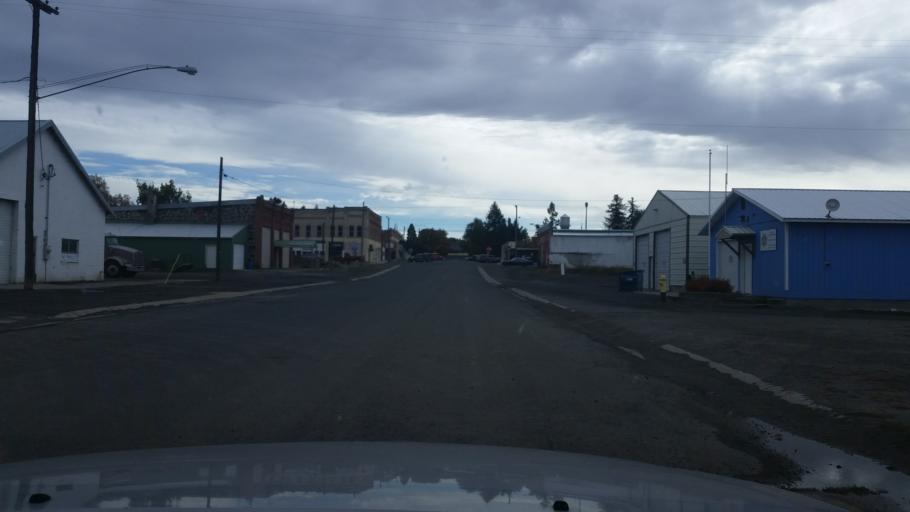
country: US
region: Washington
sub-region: Spokane County
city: Medical Lake
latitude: 47.6707
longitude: -117.8808
